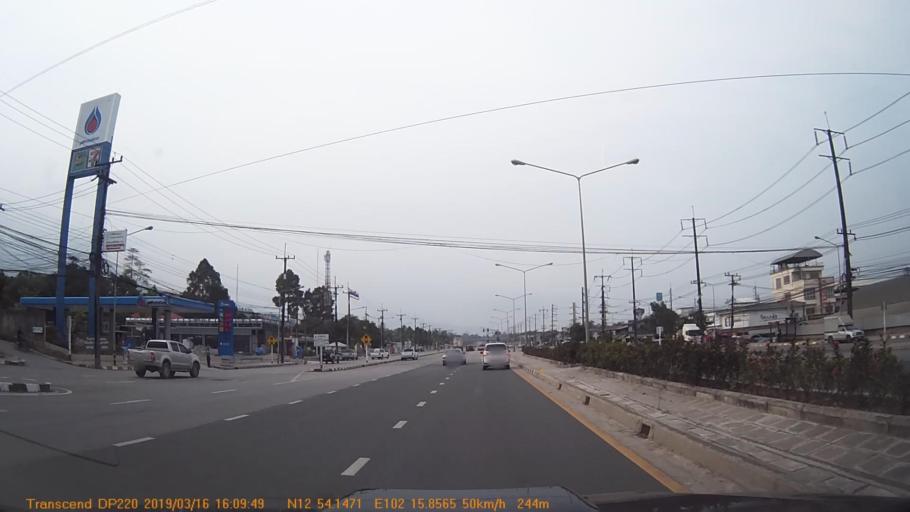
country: TH
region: Chanthaburi
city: Pong Nam Ron
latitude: 12.9026
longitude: 102.2642
